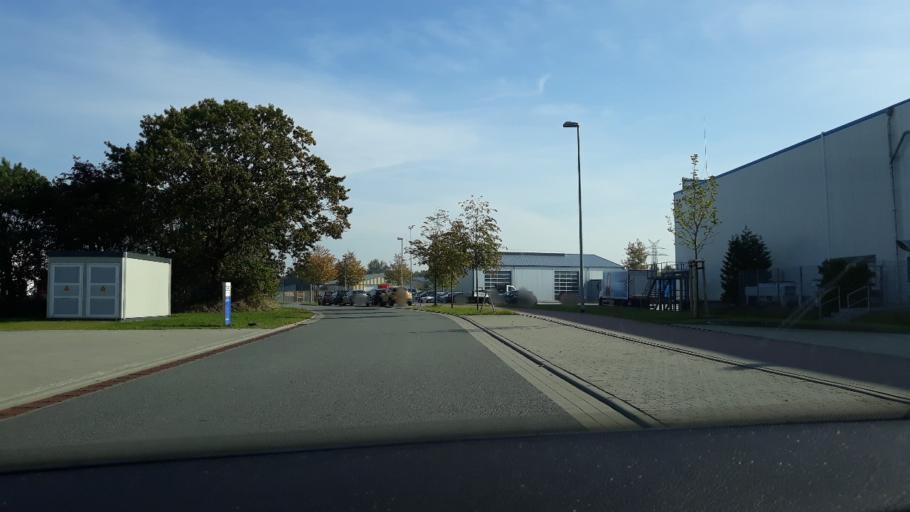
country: DE
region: Schleswig-Holstein
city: Kropp
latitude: 54.4186
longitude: 9.5232
